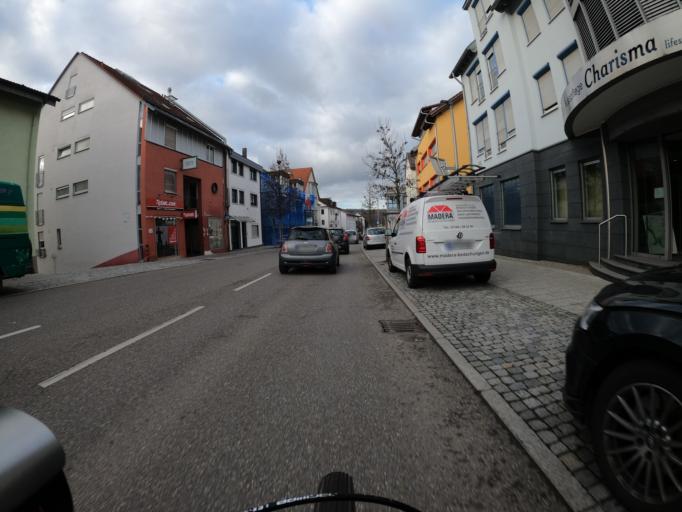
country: DE
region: Baden-Wuerttemberg
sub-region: Regierungsbezirk Stuttgart
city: Wernau
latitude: 48.6911
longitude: 9.4174
